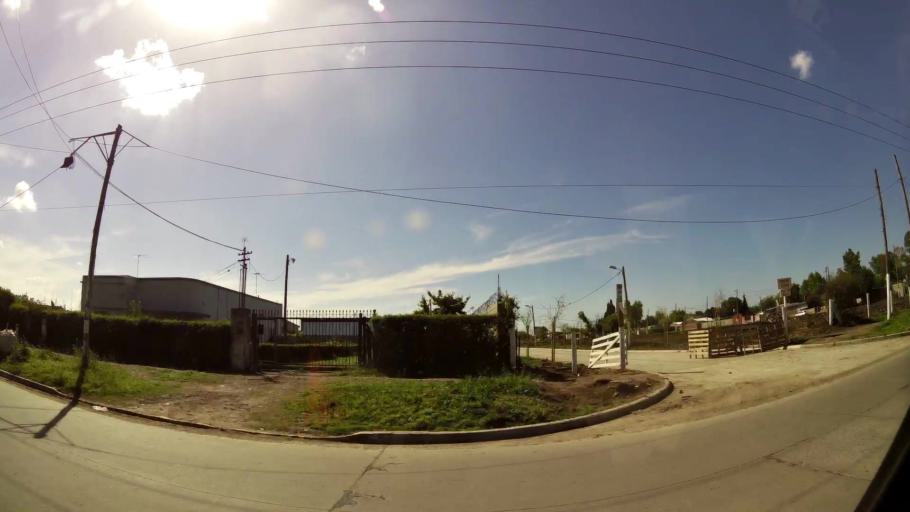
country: AR
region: Buenos Aires
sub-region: Partido de Quilmes
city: Quilmes
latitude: -34.7969
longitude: -58.2579
